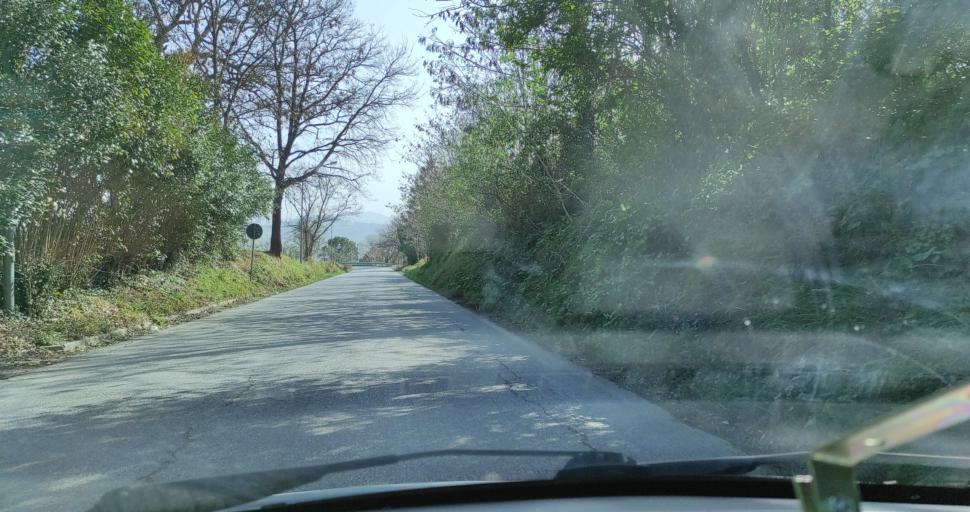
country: IT
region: The Marches
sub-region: Provincia di Macerata
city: Loro Piceno
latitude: 43.1621
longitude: 13.4249
